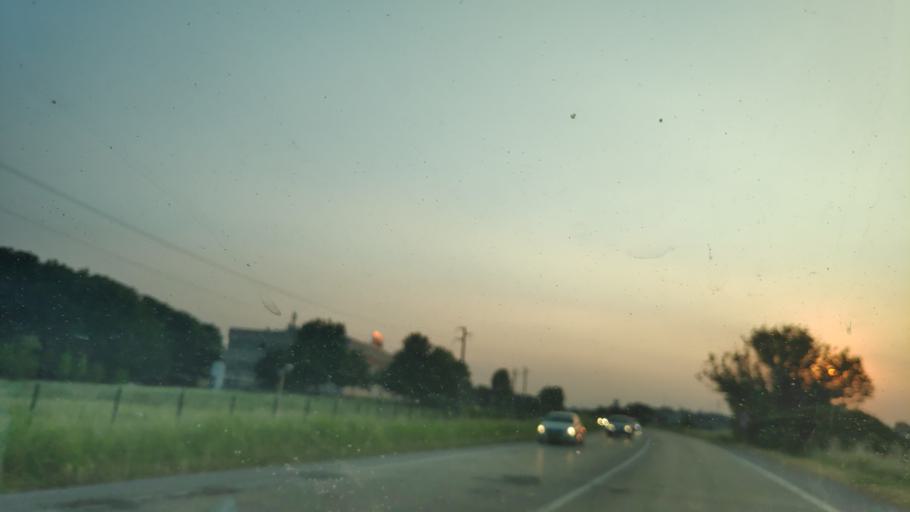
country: IT
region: Lombardy
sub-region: Citta metropolitana di Milano
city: Paullo
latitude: 45.4270
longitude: 9.3978
